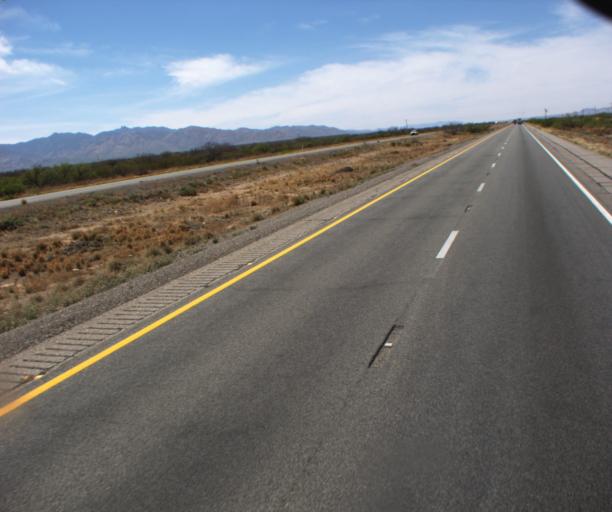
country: US
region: Arizona
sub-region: Cochise County
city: Willcox
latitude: 32.3007
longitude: -109.3681
